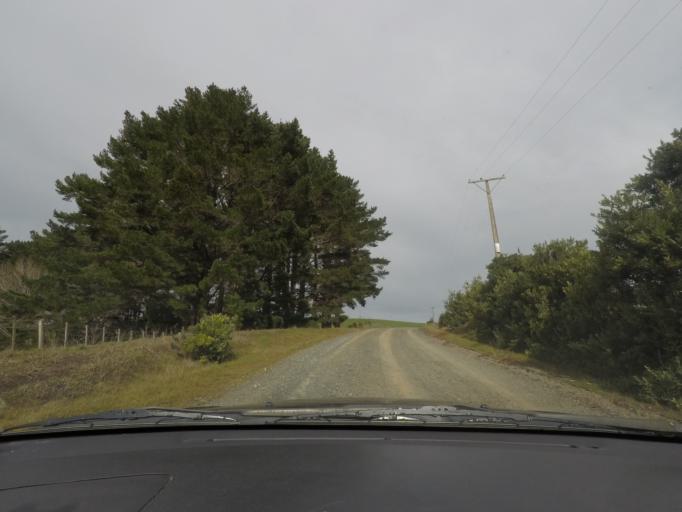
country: NZ
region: Auckland
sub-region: Auckland
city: Warkworth
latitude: -36.4529
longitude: 174.7507
